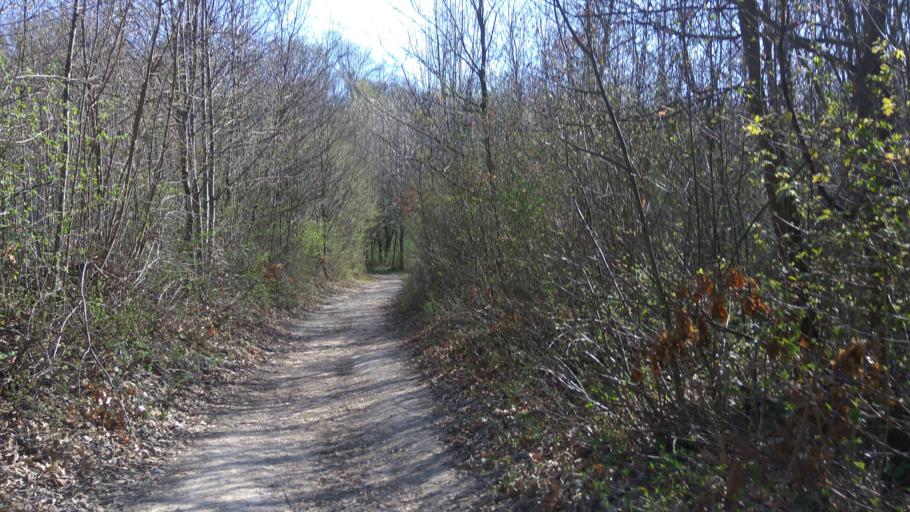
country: HU
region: Pest
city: Budakeszi
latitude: 47.4927
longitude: 18.9404
